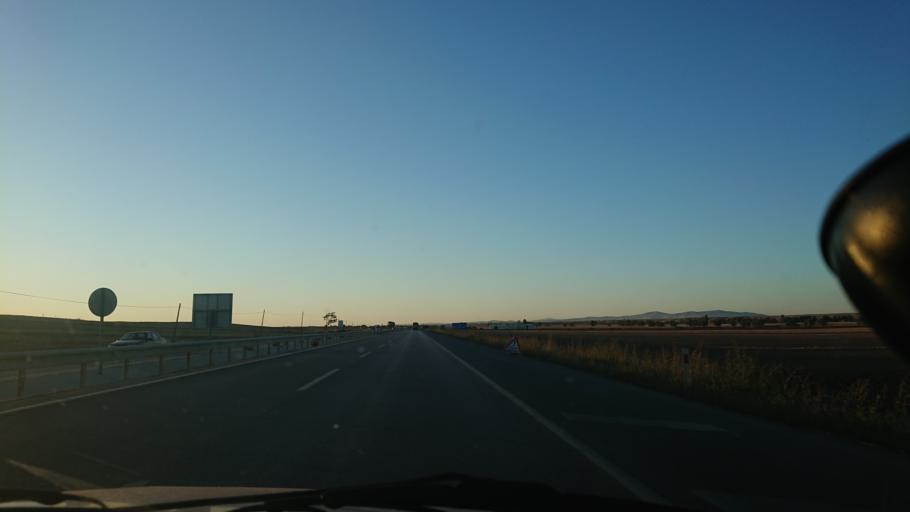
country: TR
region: Eskisehir
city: Mahmudiye
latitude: 39.5213
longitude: 30.9594
